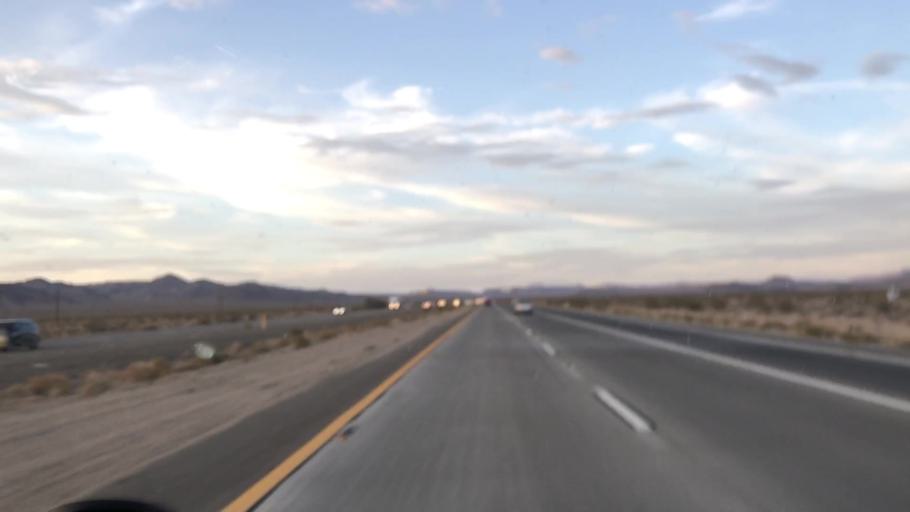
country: US
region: Nevada
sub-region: Clark County
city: Sandy Valley
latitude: 35.3122
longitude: -116.0010
